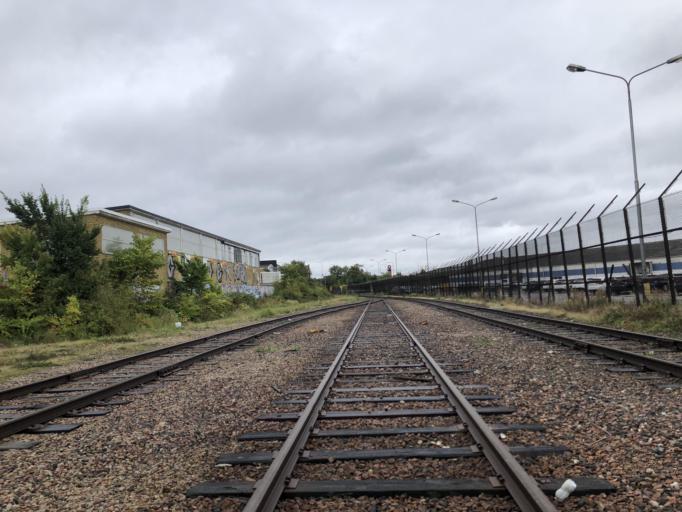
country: SE
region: Skane
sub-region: Malmo
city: Malmoe
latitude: 55.6163
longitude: 13.0178
